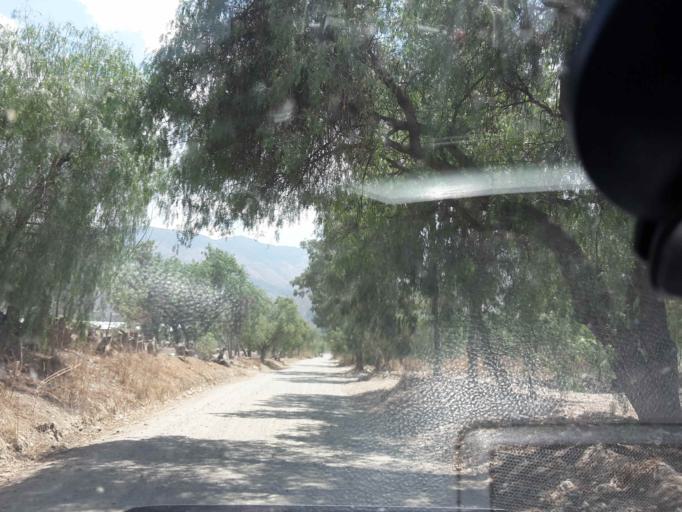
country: BO
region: Cochabamba
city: Cochabamba
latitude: -17.3410
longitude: -66.2123
